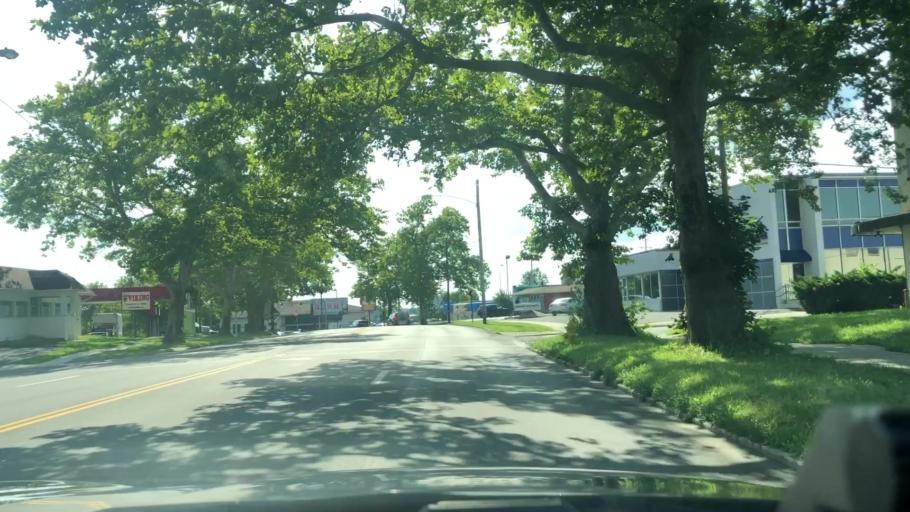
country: US
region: Pennsylvania
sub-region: Lehigh County
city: Fullerton
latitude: 40.6241
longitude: -75.4479
